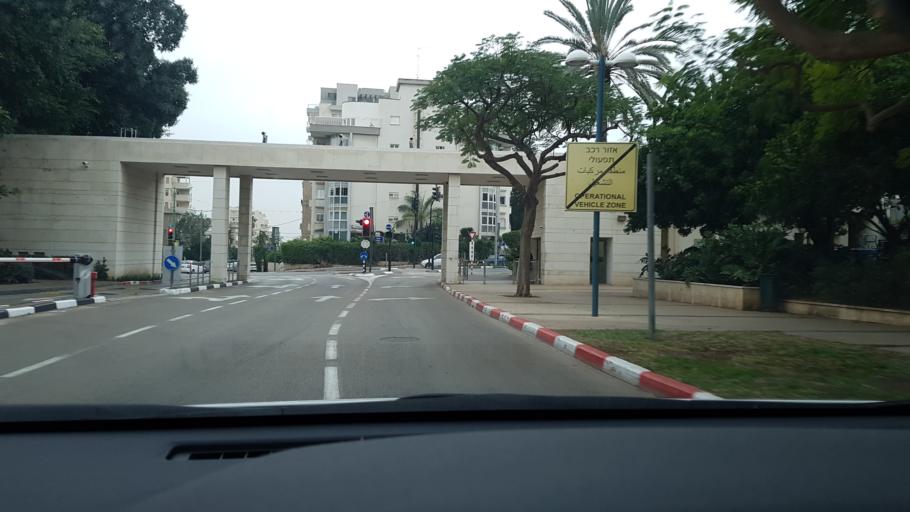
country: IL
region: Central District
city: Ness Ziona
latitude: 31.9040
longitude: 34.8084
